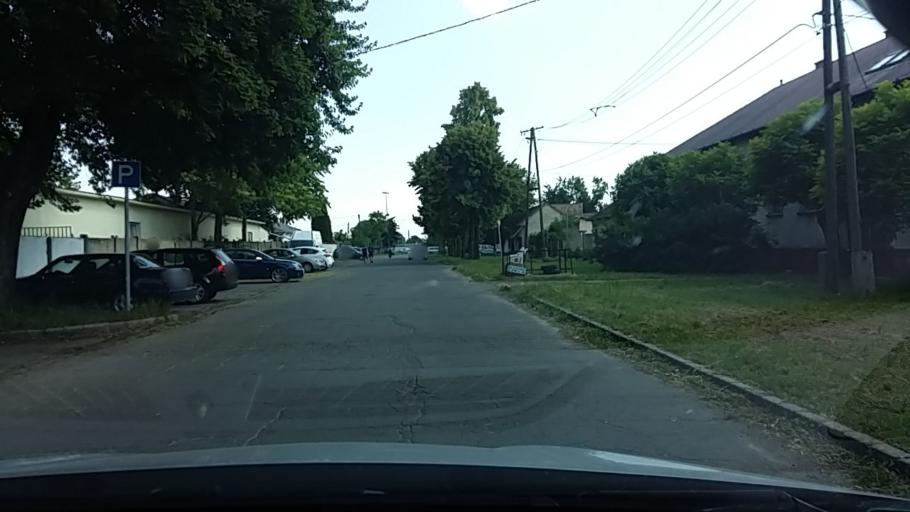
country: HU
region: Heves
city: Gyongyos
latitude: 47.7798
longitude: 19.9329
